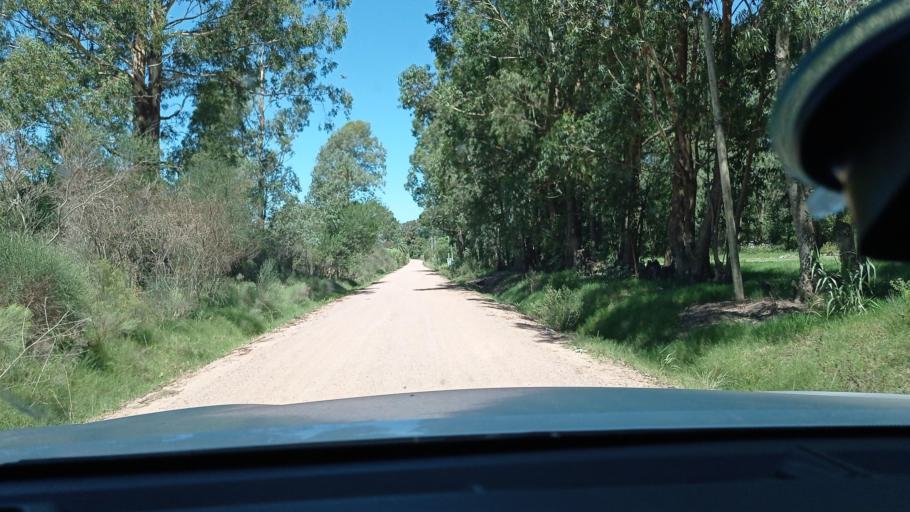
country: UY
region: Canelones
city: La Paz
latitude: -34.7588
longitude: -56.1814
